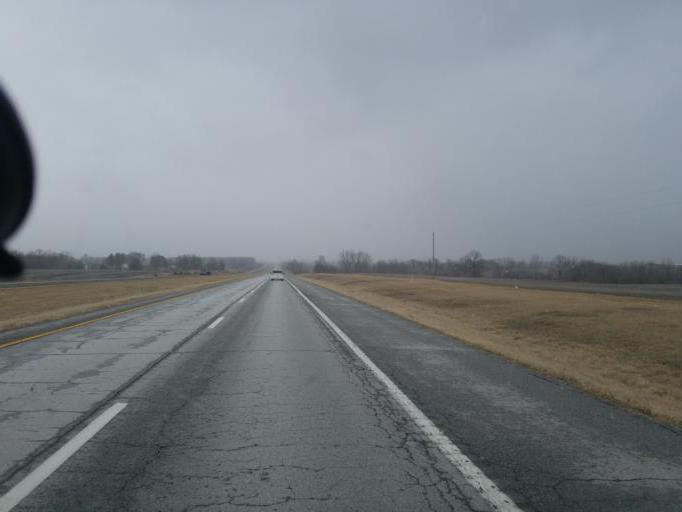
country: US
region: Missouri
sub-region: Macon County
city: La Plata
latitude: 40.0054
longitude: -92.4754
